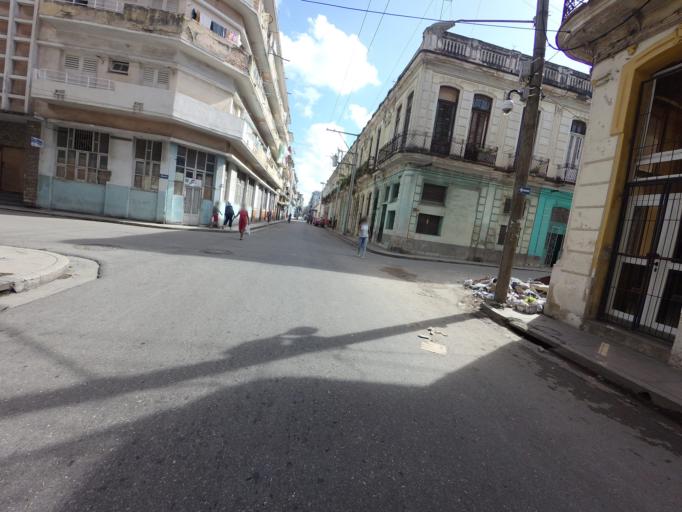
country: CU
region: La Habana
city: Centro Habana
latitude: 23.1360
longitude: -82.3718
